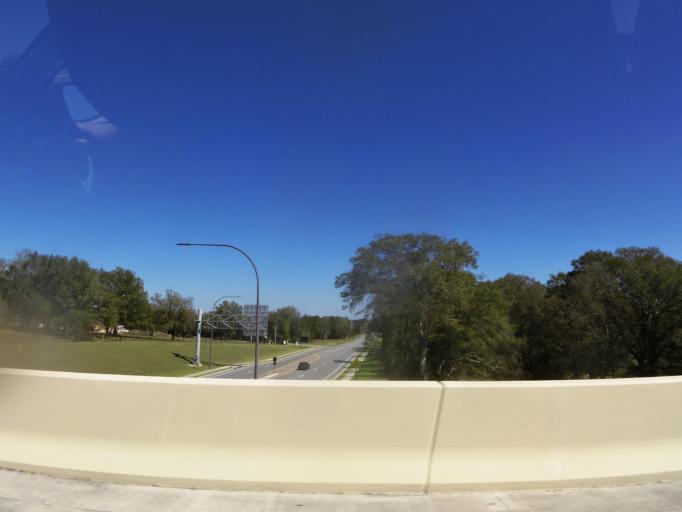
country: US
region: Florida
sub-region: Lake County
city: Mount Plymouth
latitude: 28.8009
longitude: -81.5861
